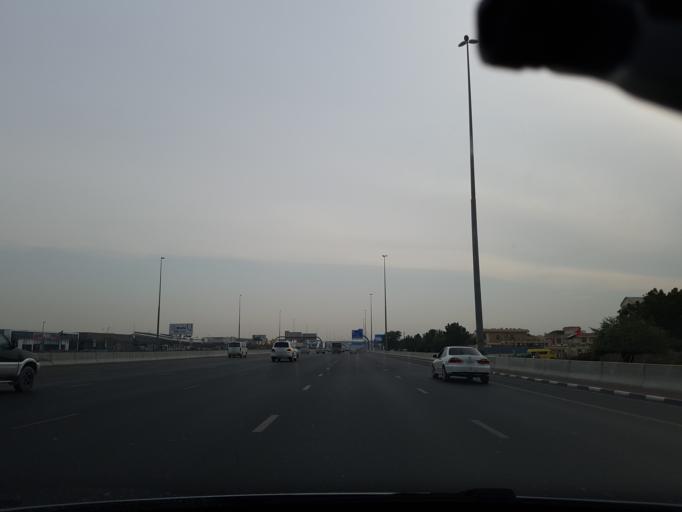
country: AE
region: Ash Shariqah
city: Sharjah
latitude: 25.3526
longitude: 55.4782
